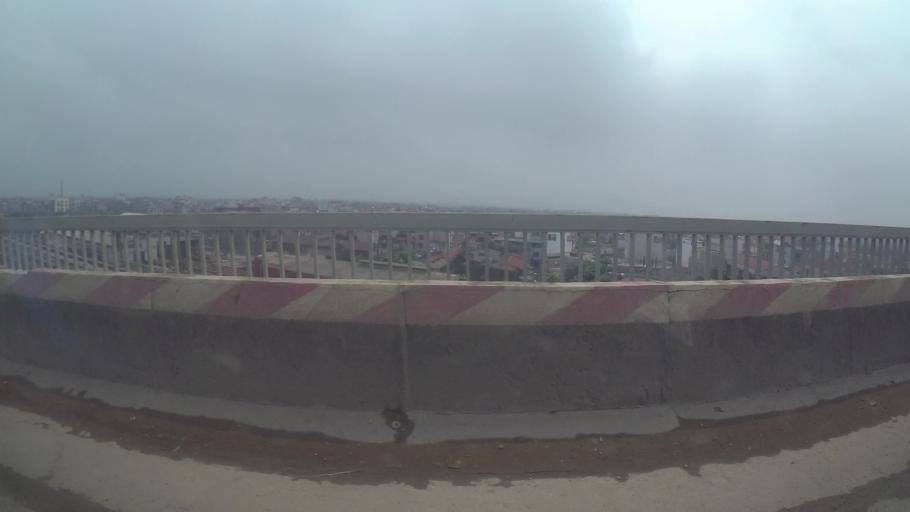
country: VN
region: Ha Noi
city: Tay Ho
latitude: 21.1094
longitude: 105.7871
